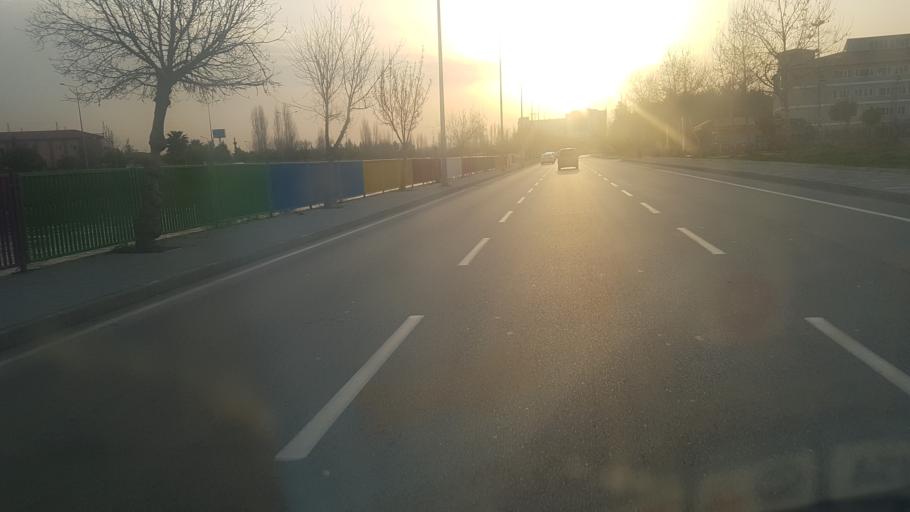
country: TR
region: Adana
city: Adana
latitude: 37.0128
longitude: 35.3465
